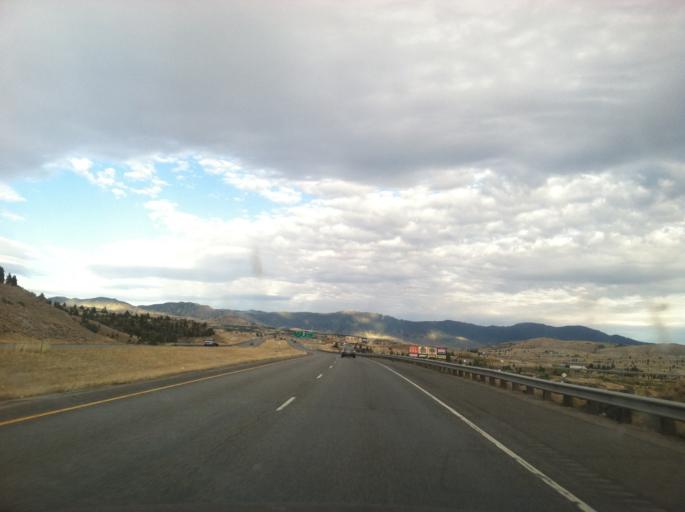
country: US
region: Montana
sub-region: Silver Bow County
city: Butte-Silver Bow (Balance)
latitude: 46.0069
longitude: -112.6546
